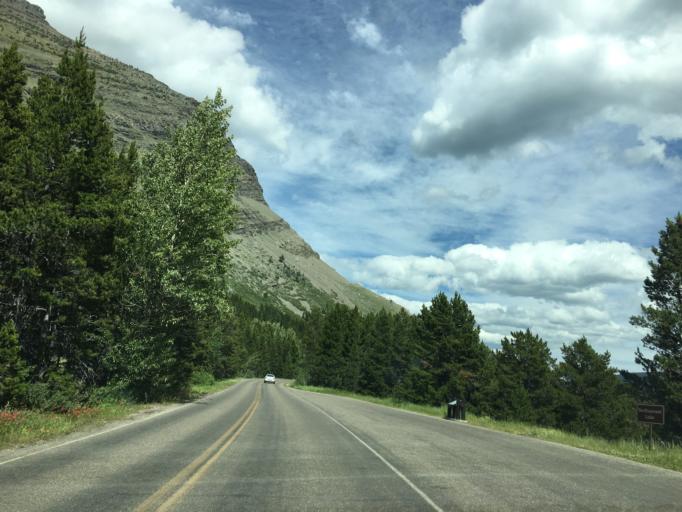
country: CA
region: Alberta
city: Cardston
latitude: 48.7996
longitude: -113.6642
